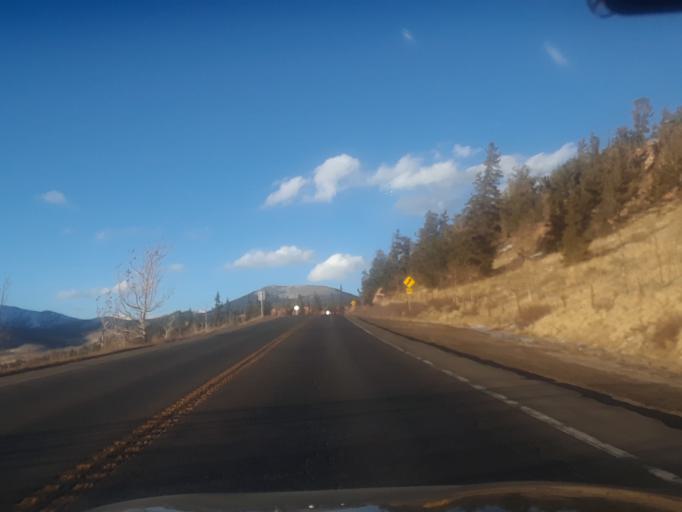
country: US
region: Colorado
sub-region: Park County
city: Fairplay
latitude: 39.2595
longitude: -105.9623
